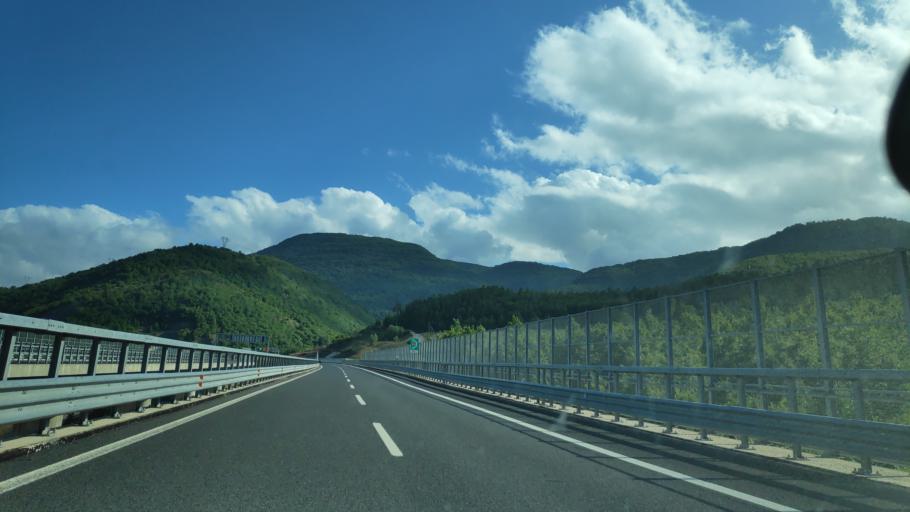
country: IT
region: Campania
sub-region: Provincia di Salerno
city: Casalbuono
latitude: 40.2206
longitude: 15.6718
